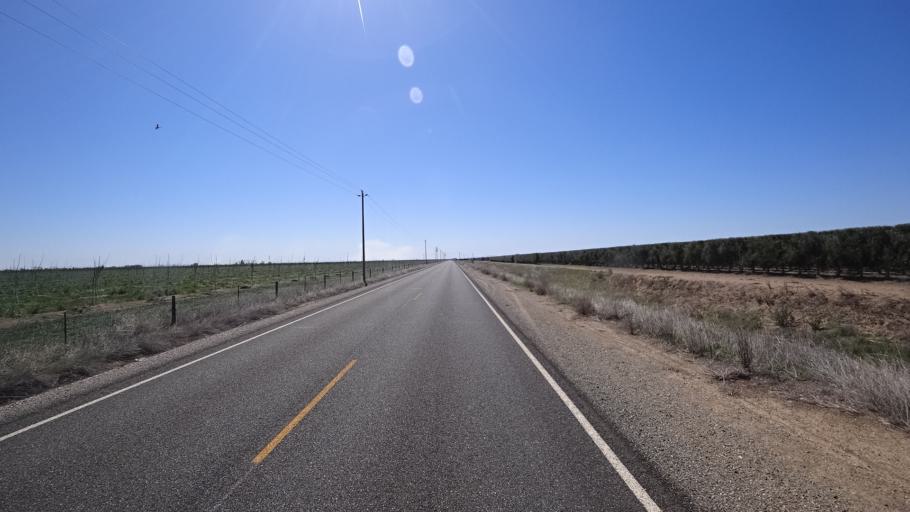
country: US
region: California
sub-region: Glenn County
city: Willows
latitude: 39.6018
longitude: -122.2498
